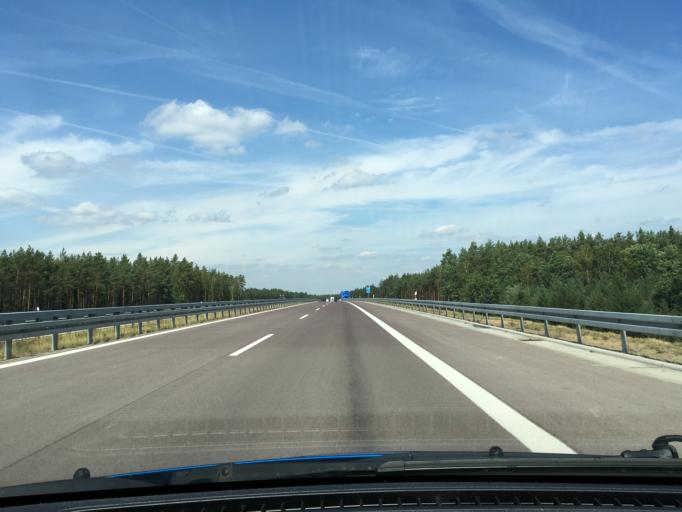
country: DE
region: Mecklenburg-Vorpommern
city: Gross Laasch
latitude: 53.3352
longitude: 11.5245
